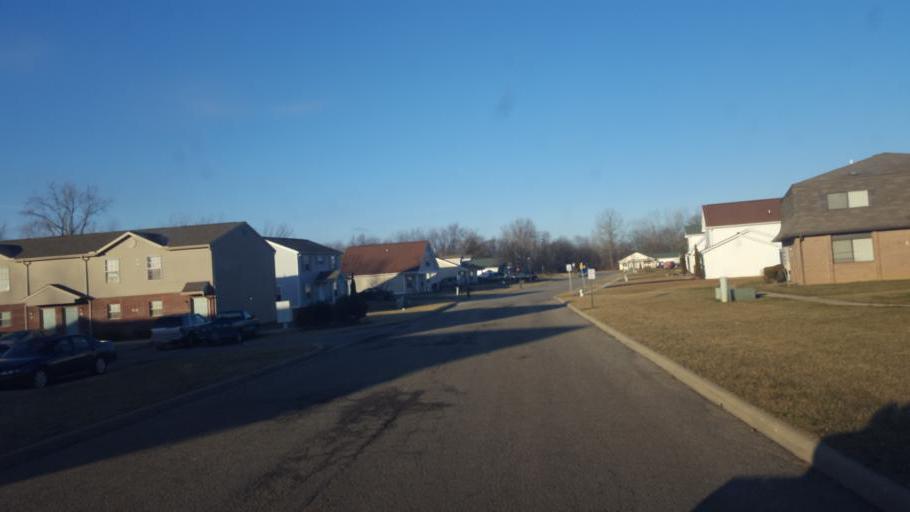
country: US
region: Ohio
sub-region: Morrow County
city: Mount Gilead
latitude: 40.5533
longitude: -82.8462
